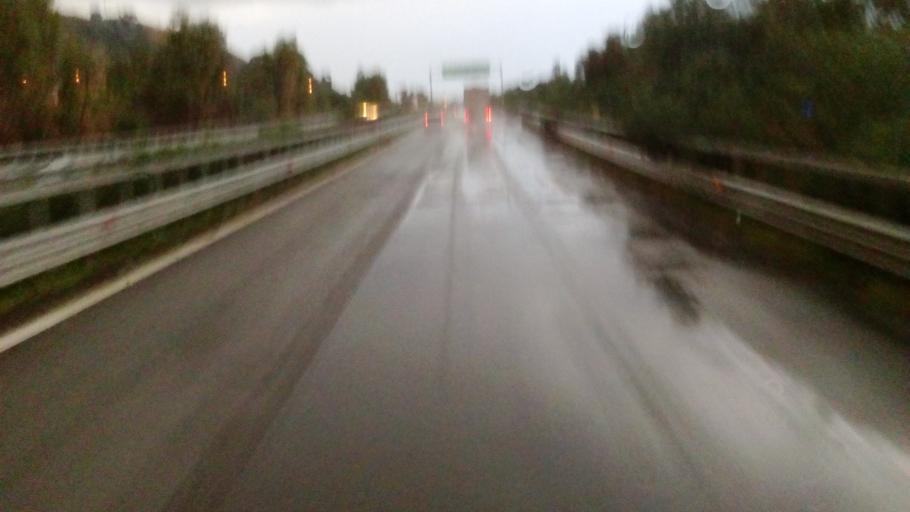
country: IT
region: Sicily
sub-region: Messina
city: Larderia
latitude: 38.1147
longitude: 15.5113
